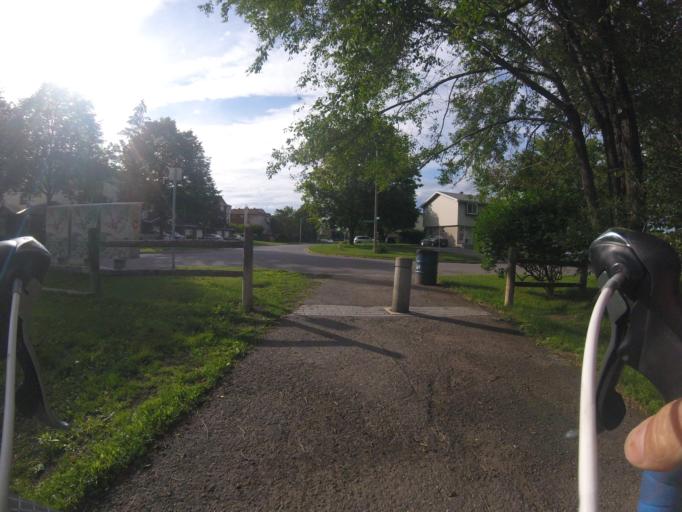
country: CA
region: Ontario
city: Bells Corners
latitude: 45.3304
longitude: -75.7482
